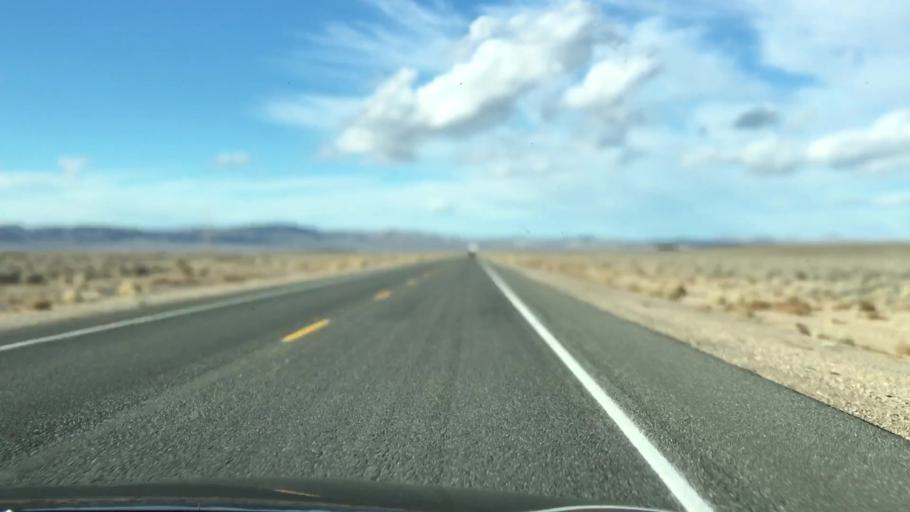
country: US
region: Nevada
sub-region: Esmeralda County
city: Goldfield
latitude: 37.4102
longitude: -117.1525
